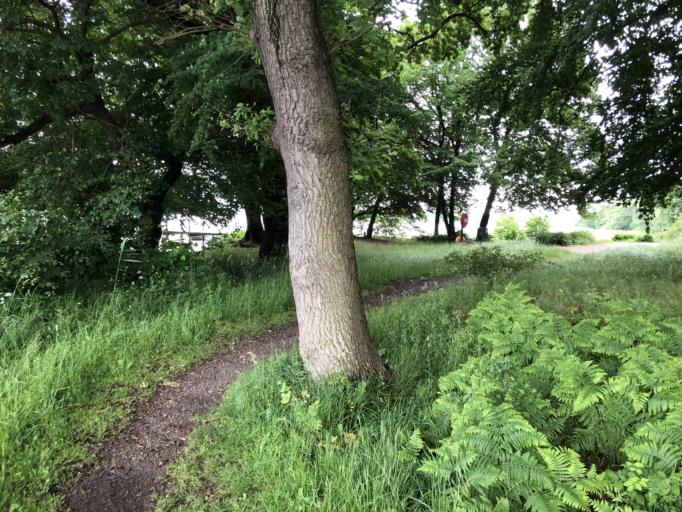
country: DK
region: Capital Region
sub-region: Gladsaxe Municipality
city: Buddinge
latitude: 55.7728
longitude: 12.4523
